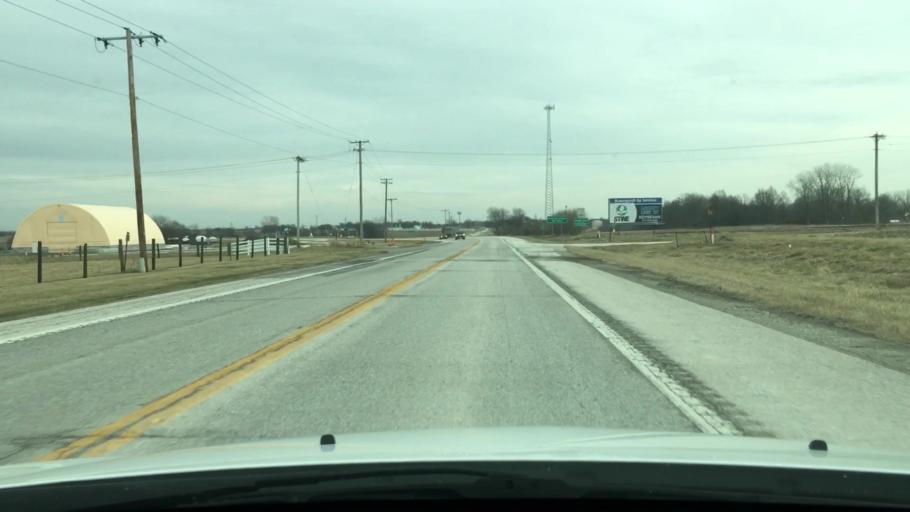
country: US
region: Missouri
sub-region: Pike County
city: Bowling Green
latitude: 39.3443
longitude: -91.2381
